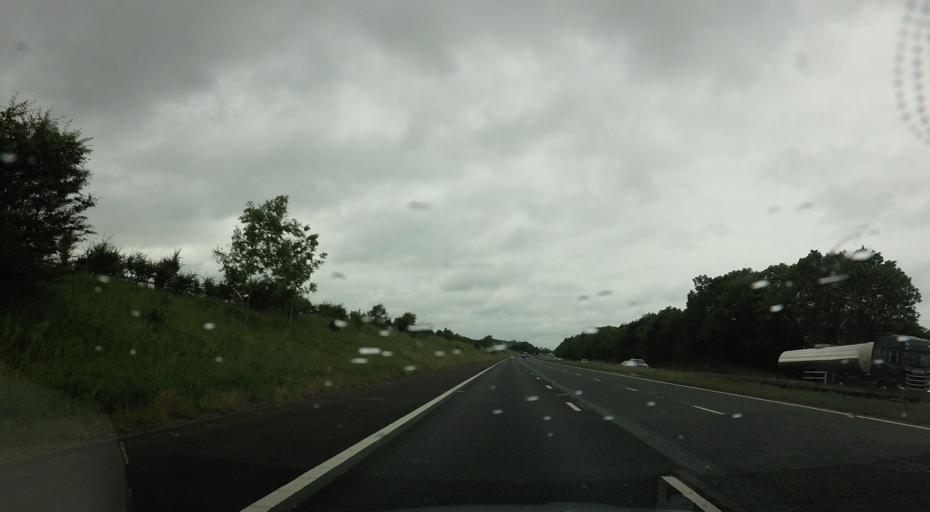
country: GB
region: England
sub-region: Cumbria
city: Penrith
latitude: 54.7155
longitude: -2.7971
